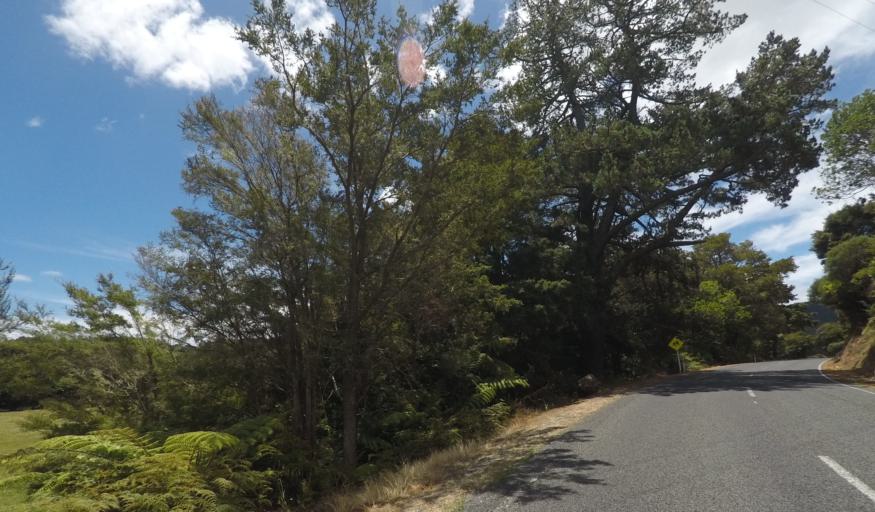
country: NZ
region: Northland
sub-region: Whangarei
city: Ngunguru
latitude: -35.5065
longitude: 174.4239
